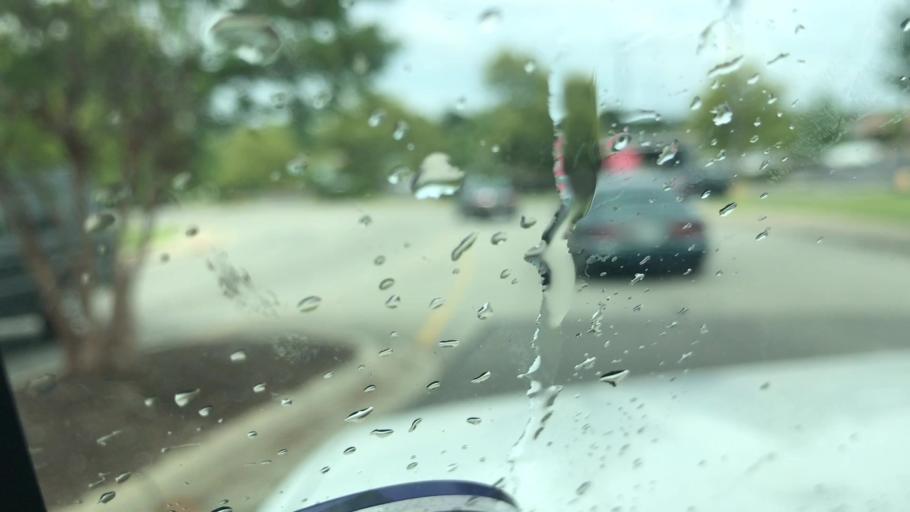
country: US
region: Virginia
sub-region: Henrico County
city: Short Pump
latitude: 37.6533
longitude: -77.6109
